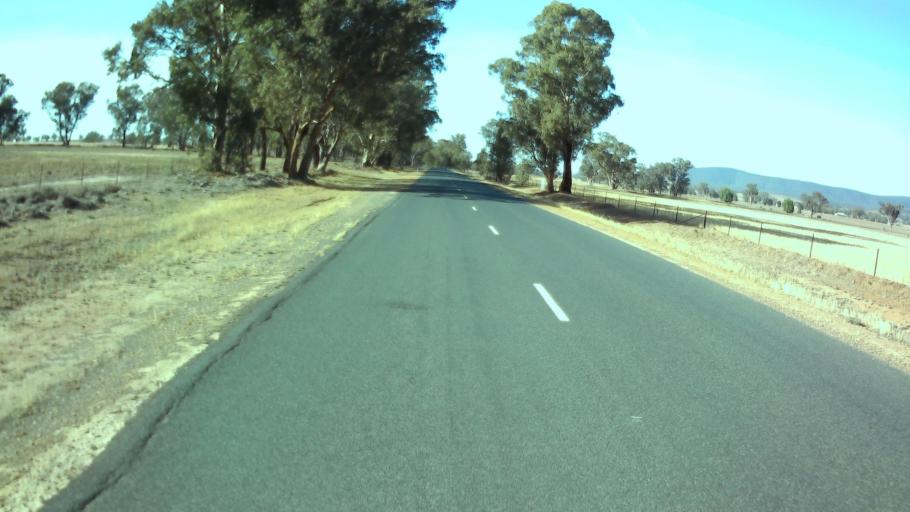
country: AU
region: New South Wales
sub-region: Weddin
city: Grenfell
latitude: -33.9260
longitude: 148.1383
